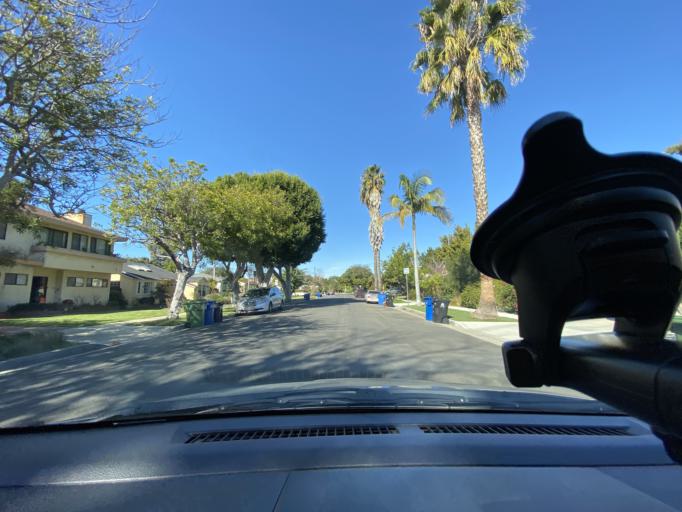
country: US
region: California
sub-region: Los Angeles County
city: Westwood, Los Angeles
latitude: 34.0349
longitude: -118.4279
